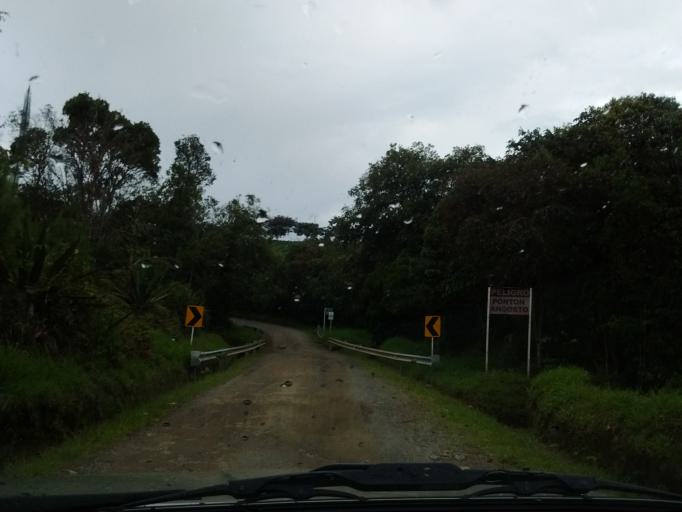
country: CO
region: Cauca
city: Cajibio
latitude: 2.5776
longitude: -76.6587
